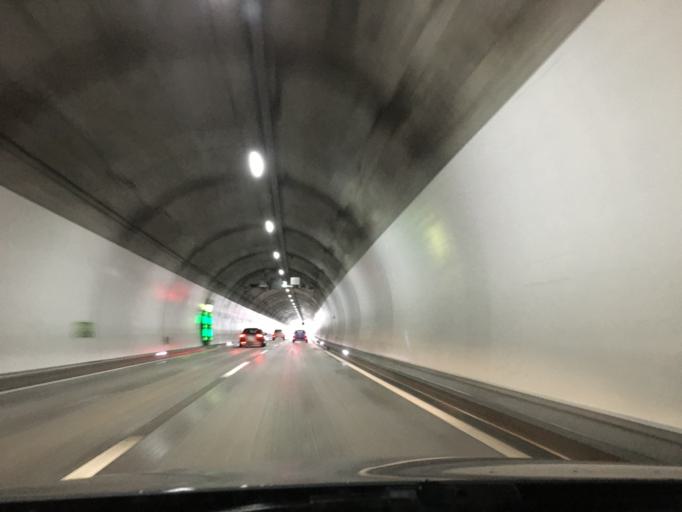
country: CH
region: Saint Gallen
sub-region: Wahlkreis Sarganserland
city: Walenstadt
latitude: 47.1096
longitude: 9.2900
